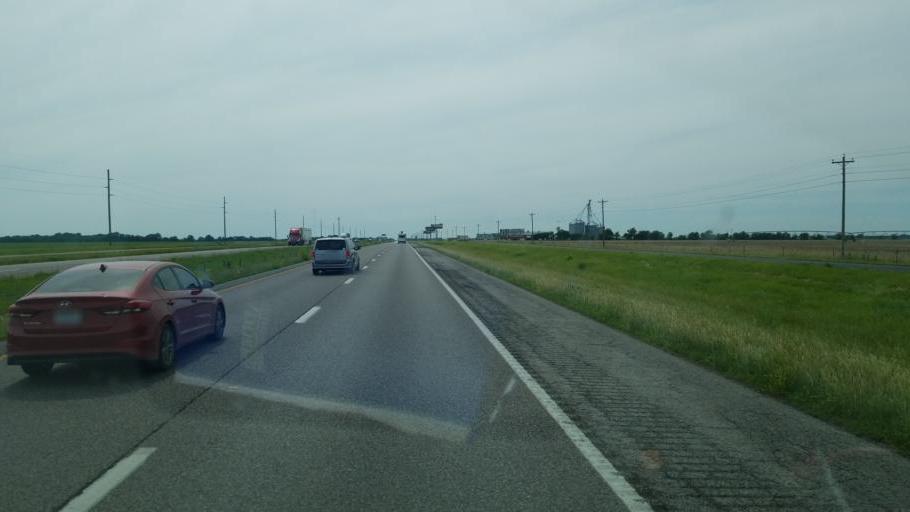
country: US
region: Missouri
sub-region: Callaway County
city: Fulton
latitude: 38.9532
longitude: -92.0663
